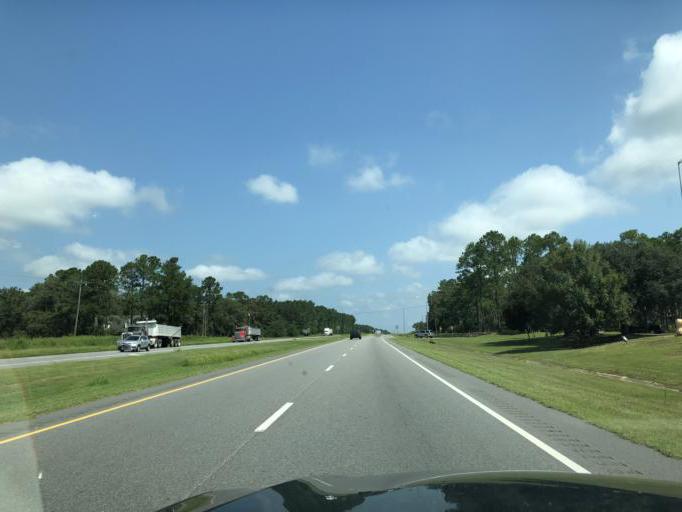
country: US
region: Alabama
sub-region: Houston County
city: Cottonwood
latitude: 31.0085
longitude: -85.4078
